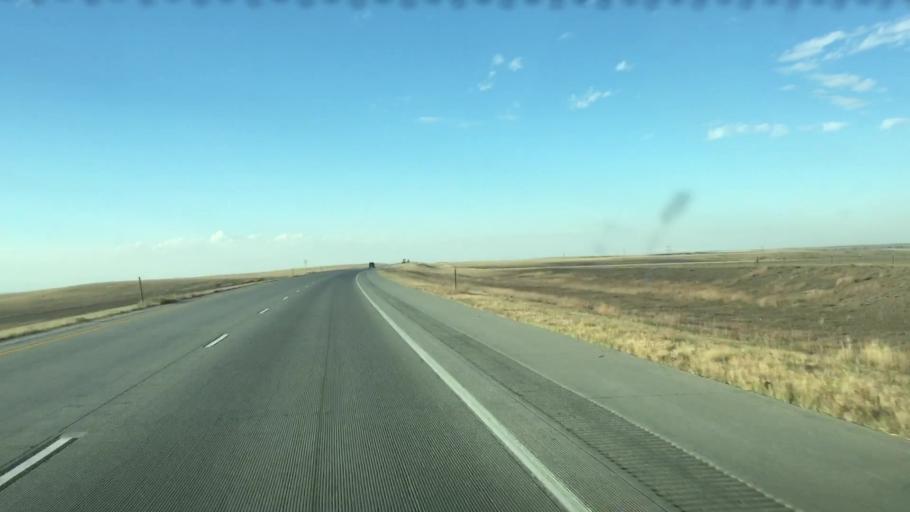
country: US
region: Colorado
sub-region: Lincoln County
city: Limon
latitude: 39.3796
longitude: -103.8859
